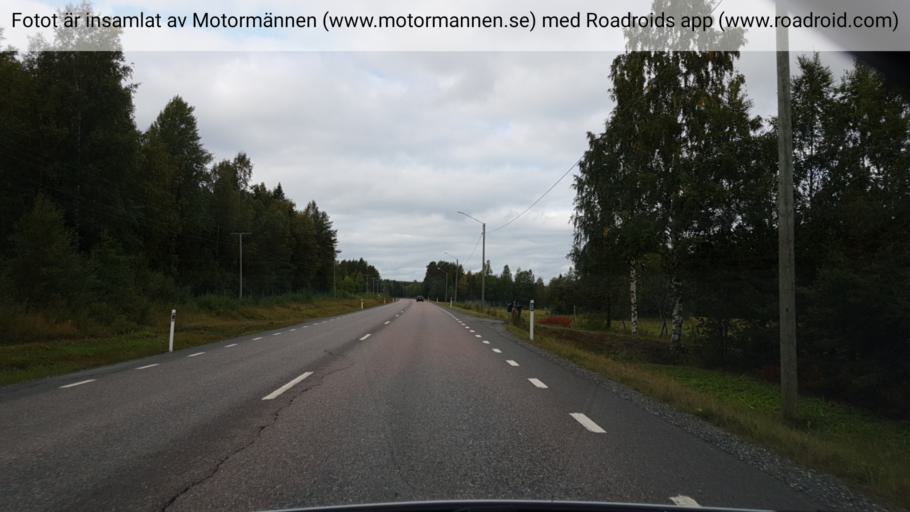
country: SE
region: Vaesterbotten
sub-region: Skelleftea Kommun
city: Forsbacka
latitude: 64.8076
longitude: 20.6766
